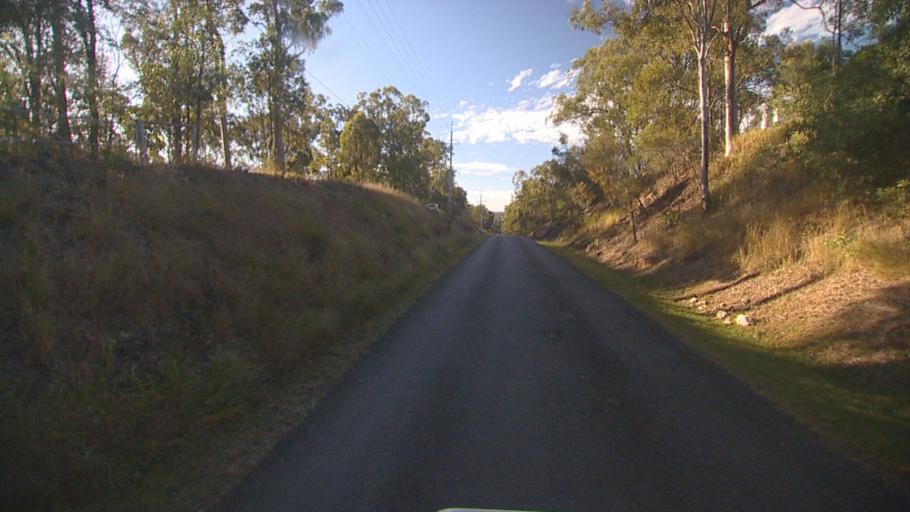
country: AU
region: Queensland
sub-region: Logan
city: Waterford West
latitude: -27.7307
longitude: 153.1521
